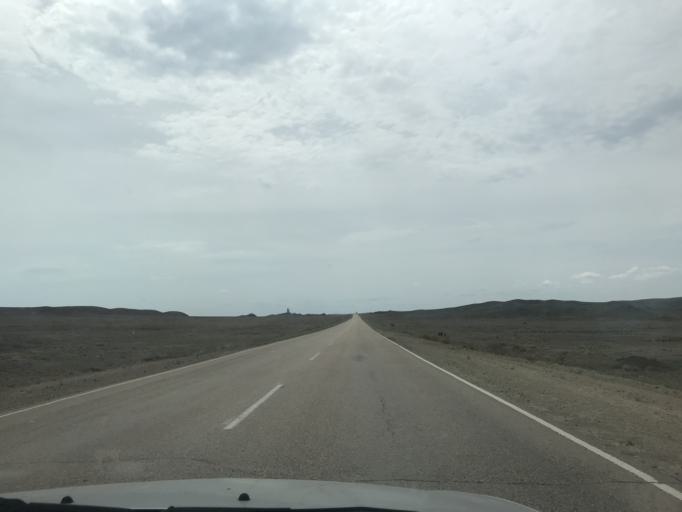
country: KZ
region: Zhambyl
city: Mynaral
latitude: 45.4310
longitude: 73.6169
